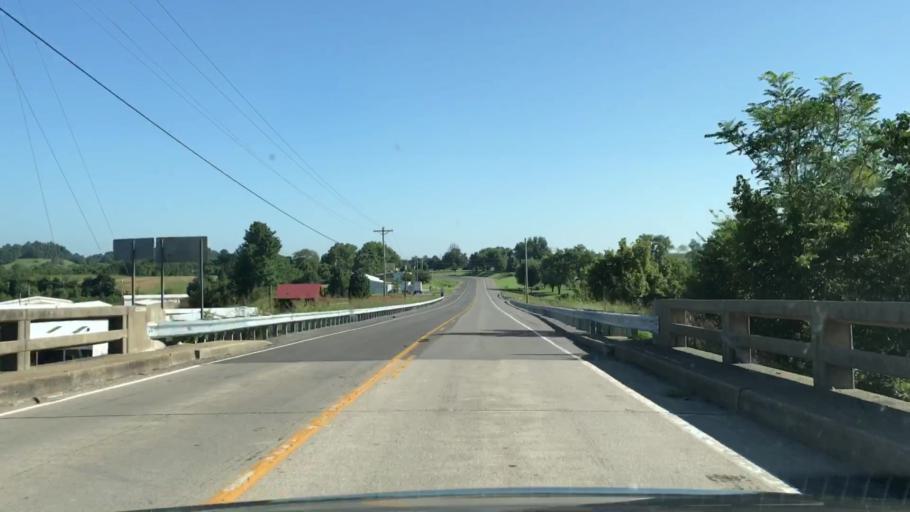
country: US
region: Kentucky
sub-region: Cumberland County
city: Burkesville
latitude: 36.7472
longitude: -85.3715
